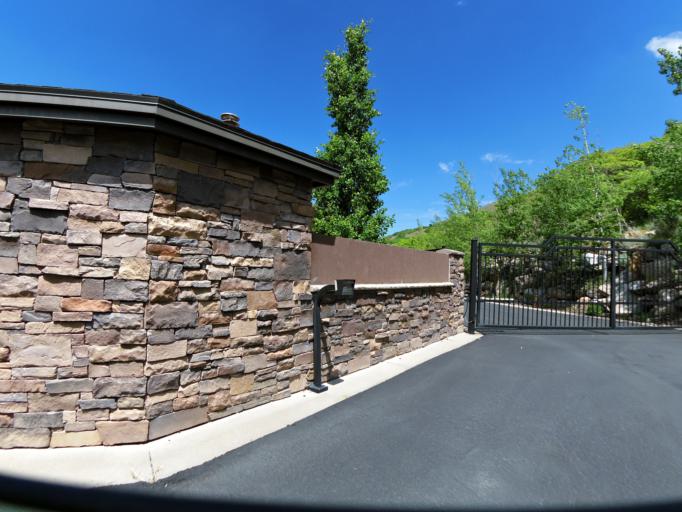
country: US
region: Utah
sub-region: Weber County
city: Uintah
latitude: 41.1736
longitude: -111.9258
